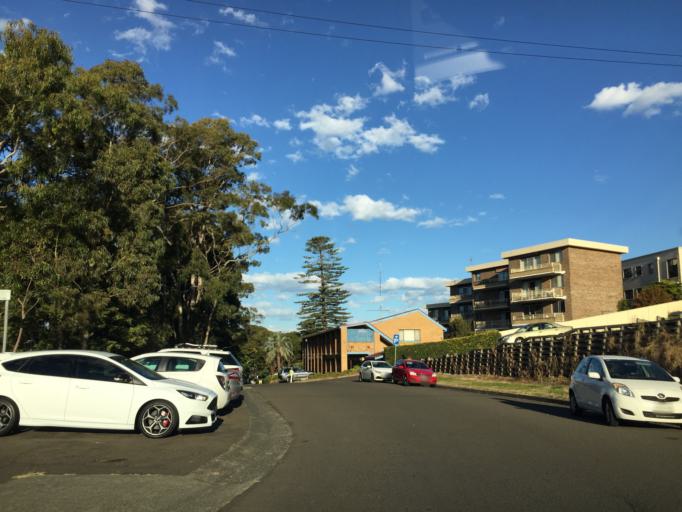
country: AU
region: New South Wales
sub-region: Kiama
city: Kiama
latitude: -34.6705
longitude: 150.8528
